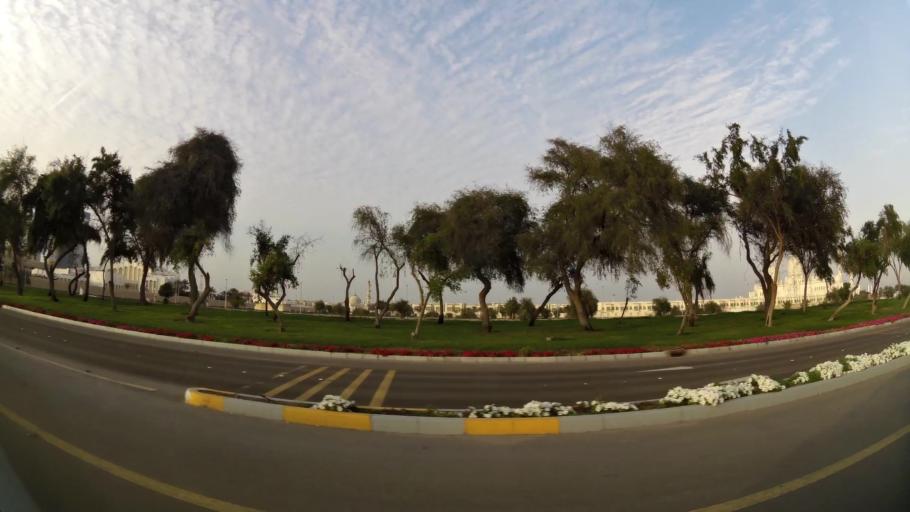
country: AE
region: Abu Dhabi
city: Abu Dhabi
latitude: 24.4088
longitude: 54.4676
